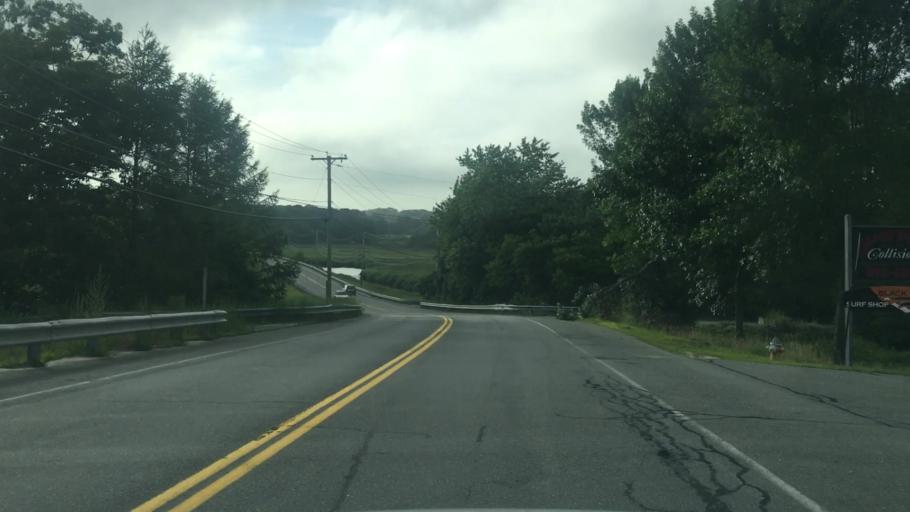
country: US
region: Maine
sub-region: Cumberland County
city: Scarborough
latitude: 43.5785
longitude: -70.3232
